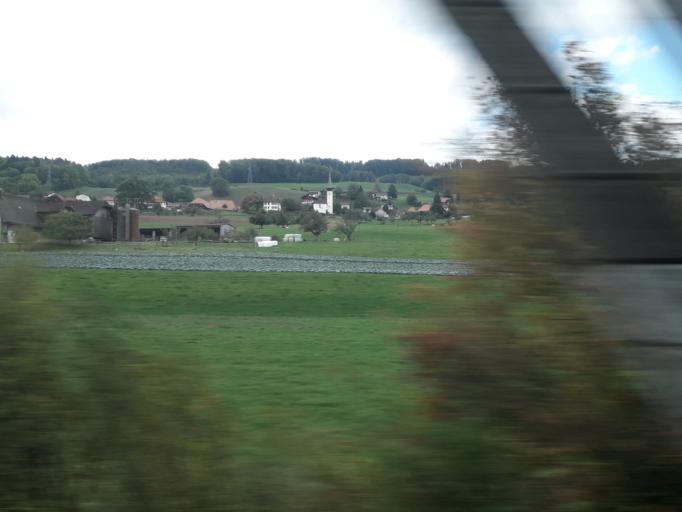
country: CH
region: Bern
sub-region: Bern-Mittelland District
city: Muhlethurnen
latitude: 46.8268
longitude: 7.5089
